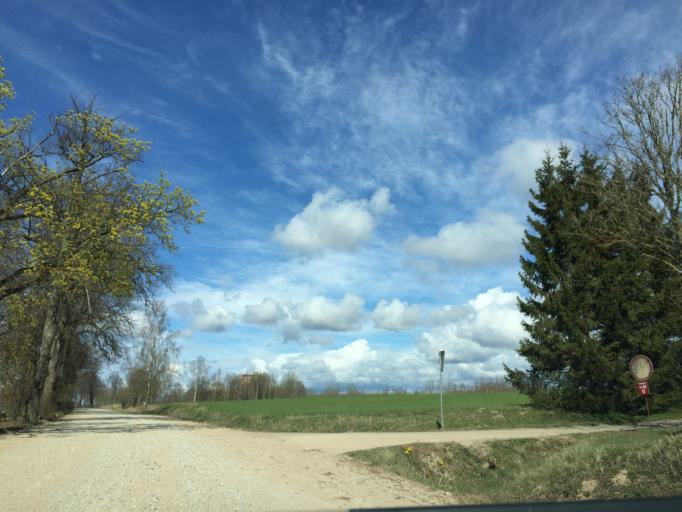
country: LV
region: Limbazu Rajons
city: Limbazi
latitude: 57.5676
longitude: 24.5928
